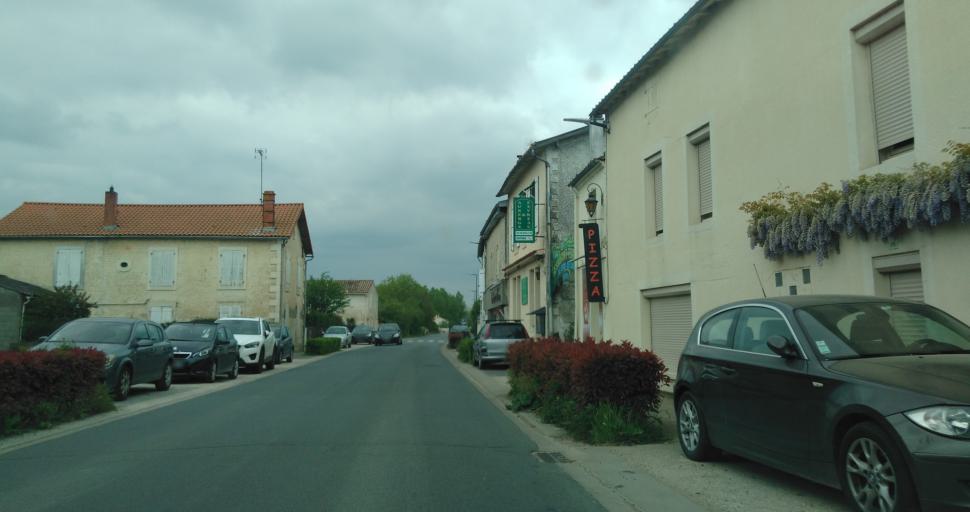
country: FR
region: Poitou-Charentes
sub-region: Departement des Deux-Sevres
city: Bessines
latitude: 46.3108
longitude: -0.5272
